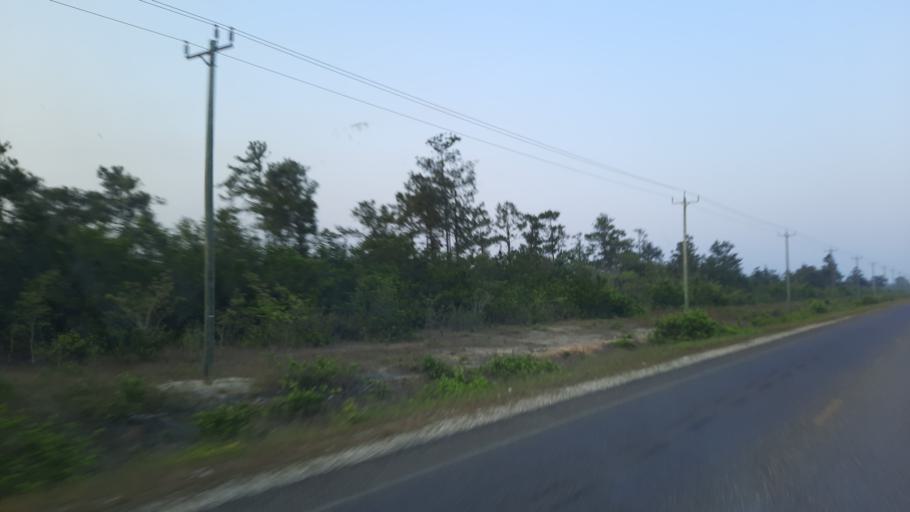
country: BZ
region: Stann Creek
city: Placencia
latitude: 16.5329
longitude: -88.4436
